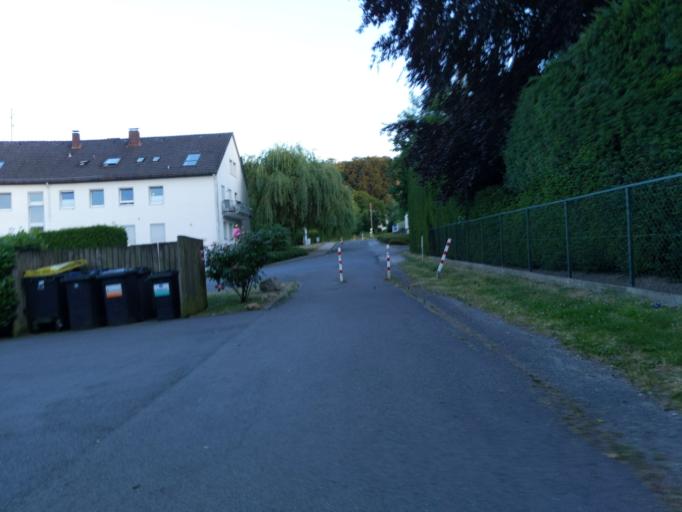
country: DE
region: North Rhine-Westphalia
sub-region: Regierungsbezirk Detmold
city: Bielefeld
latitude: 52.0230
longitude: 8.4815
